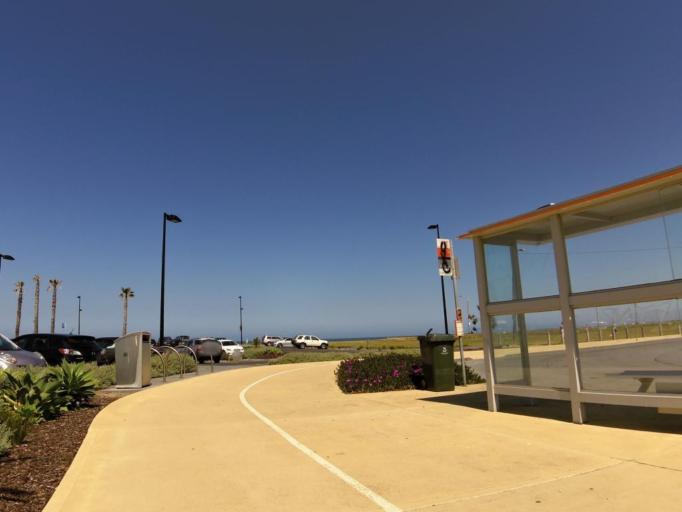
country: AU
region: Victoria
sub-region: Hobsons Bay
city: Williamstown North
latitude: -37.8676
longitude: 144.8881
